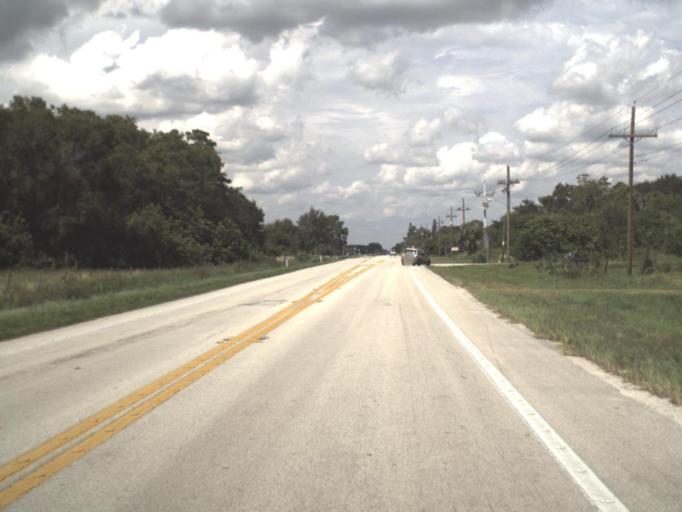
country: US
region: Florida
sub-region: Hendry County
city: LaBelle
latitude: 26.6708
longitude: -81.4364
